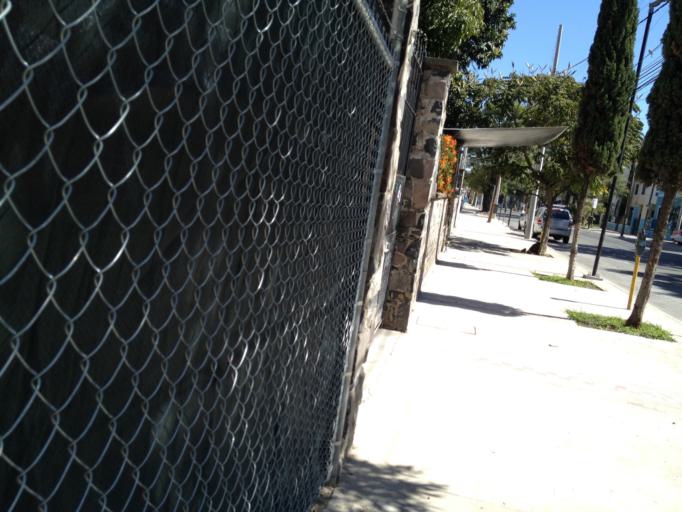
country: MX
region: Jalisco
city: Guadalajara
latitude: 20.6756
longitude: -103.3621
